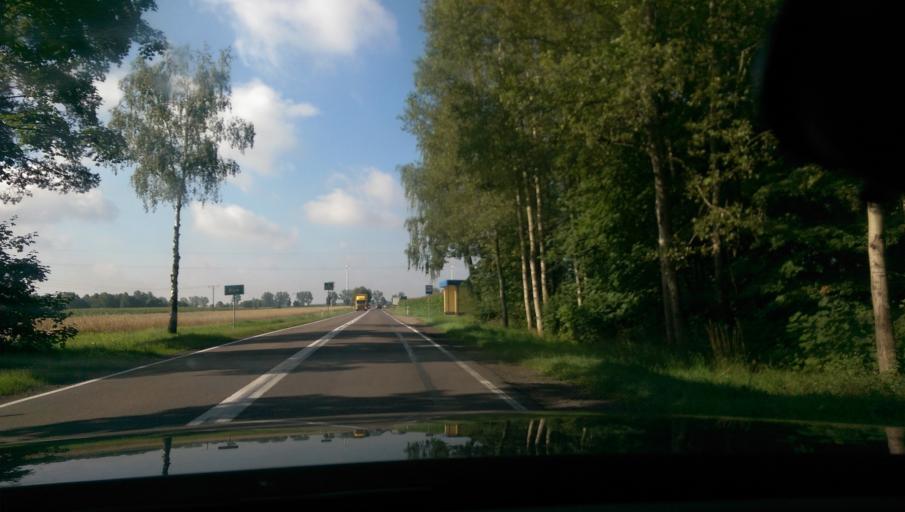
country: PL
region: Masovian Voivodeship
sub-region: Powiat plonski
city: Sochocin
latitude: 52.6712
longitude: 20.4554
